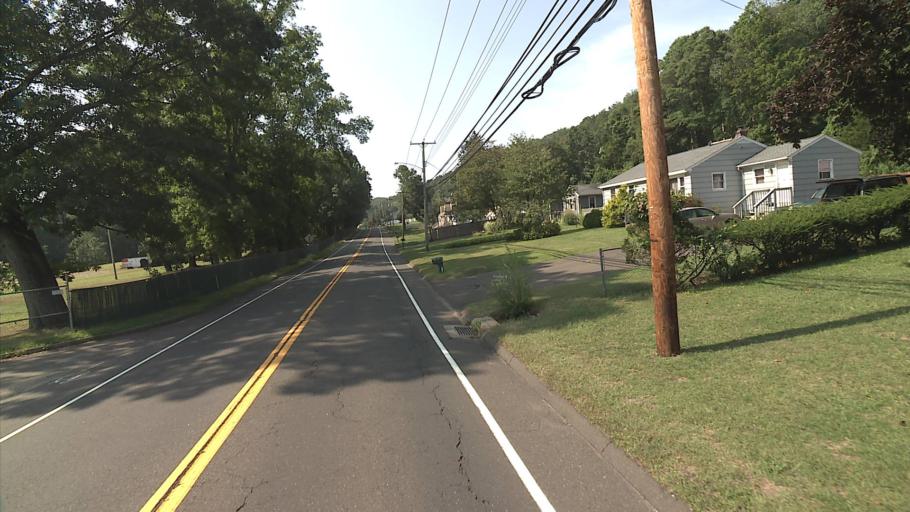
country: US
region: Connecticut
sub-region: New Haven County
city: East Haven
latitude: 41.2973
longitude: -72.8631
